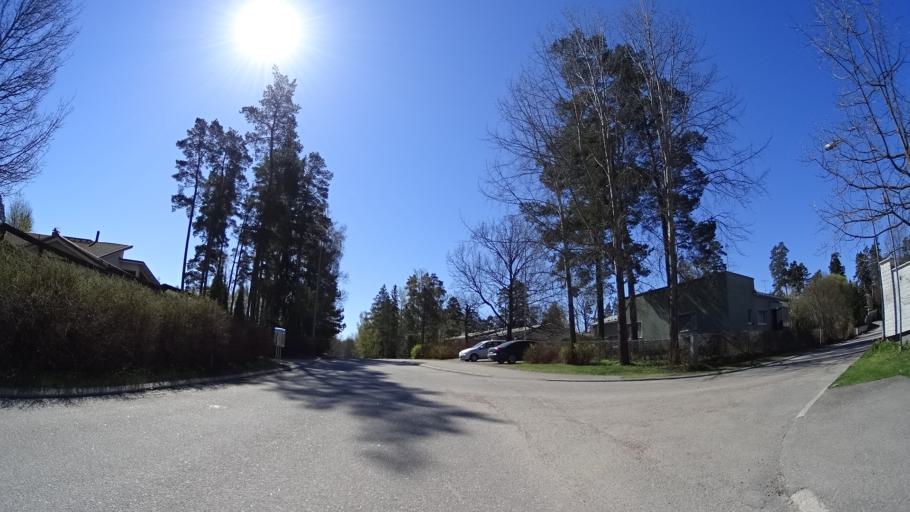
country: FI
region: Uusimaa
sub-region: Helsinki
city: Koukkuniemi
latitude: 60.1675
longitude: 24.7876
